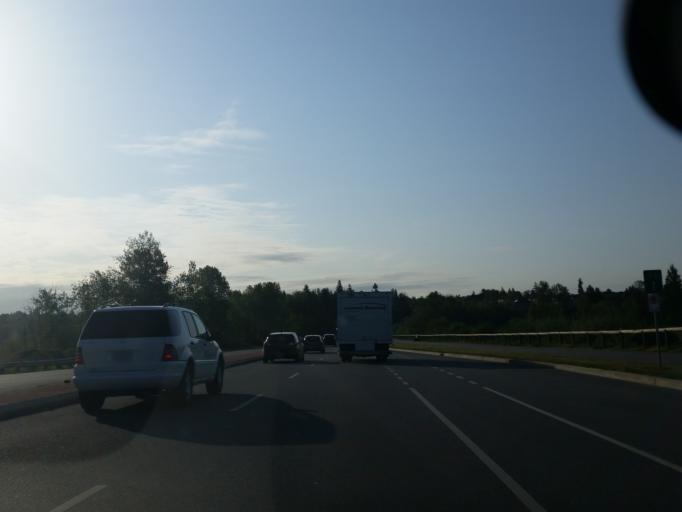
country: CA
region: British Columbia
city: Langley
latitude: 49.1374
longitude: -122.7334
